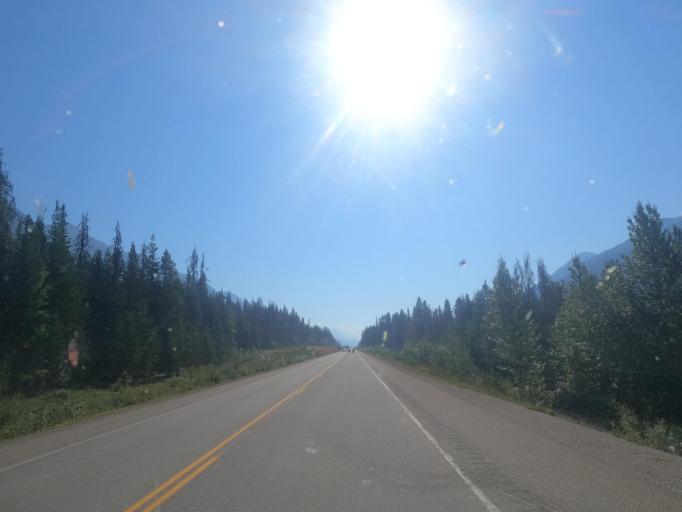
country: CA
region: Alberta
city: Grande Cache
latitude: 52.9906
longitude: -119.0106
